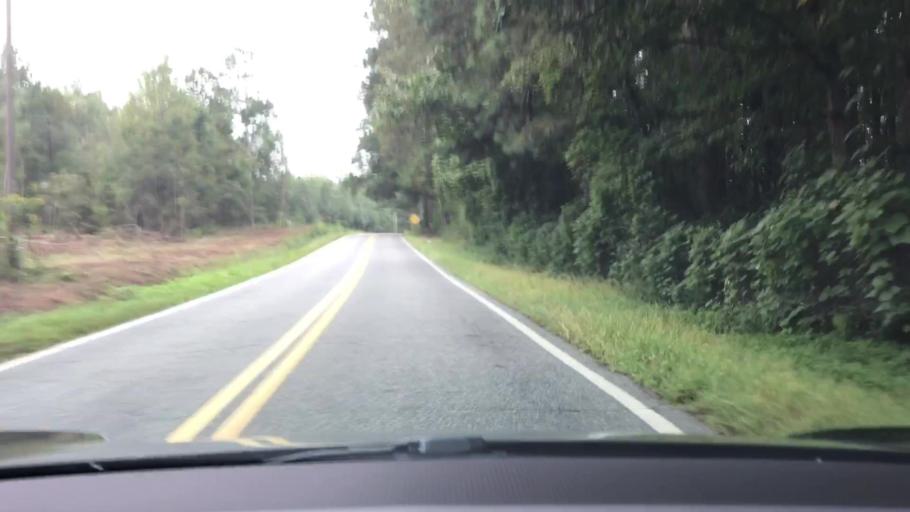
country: US
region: Georgia
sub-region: Barrow County
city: Auburn
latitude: 34.0298
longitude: -83.7813
